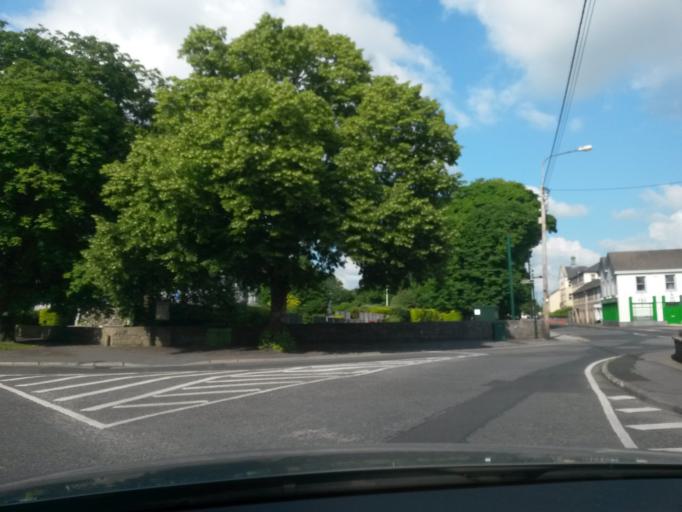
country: IE
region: Munster
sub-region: An Clar
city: Ennis
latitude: 52.8478
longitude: -8.9816
